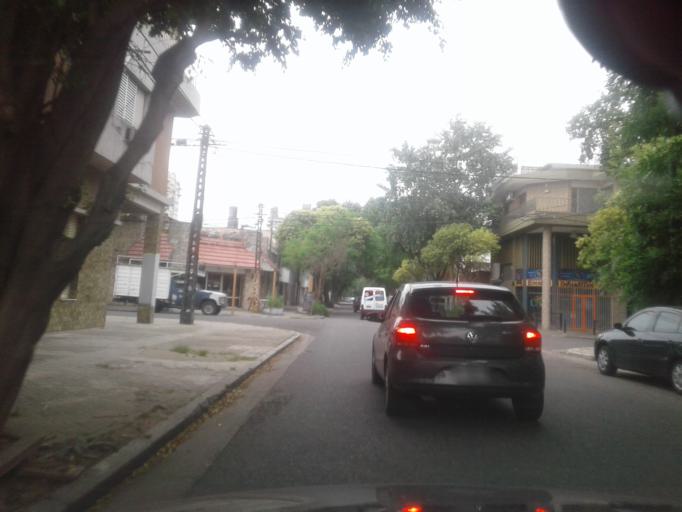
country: AR
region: Santa Fe
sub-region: Departamento de Rosario
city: Rosario
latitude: -32.9475
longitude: -60.6770
